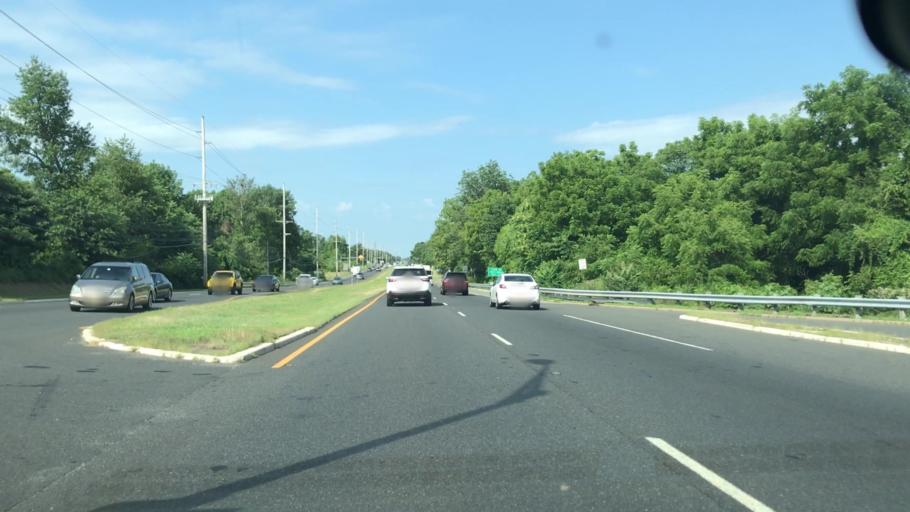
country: US
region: New Jersey
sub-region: Somerset County
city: Bradley Gardens
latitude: 40.5611
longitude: -74.7023
